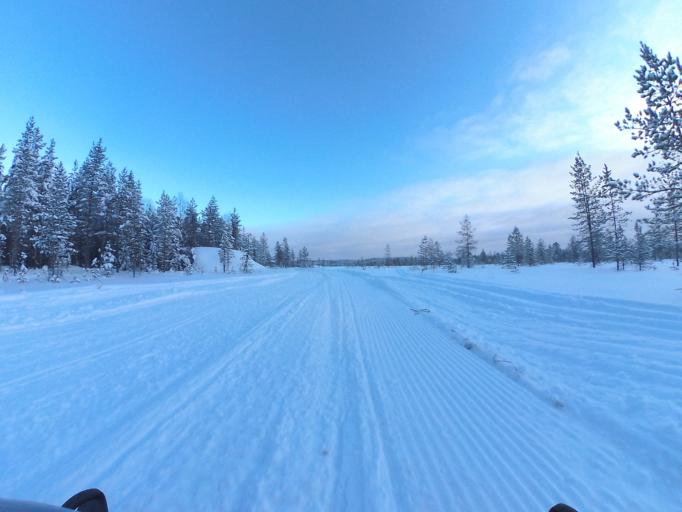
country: FI
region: Lapland
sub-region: Rovaniemi
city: Rovaniemi
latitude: 66.5136
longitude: 25.9855
